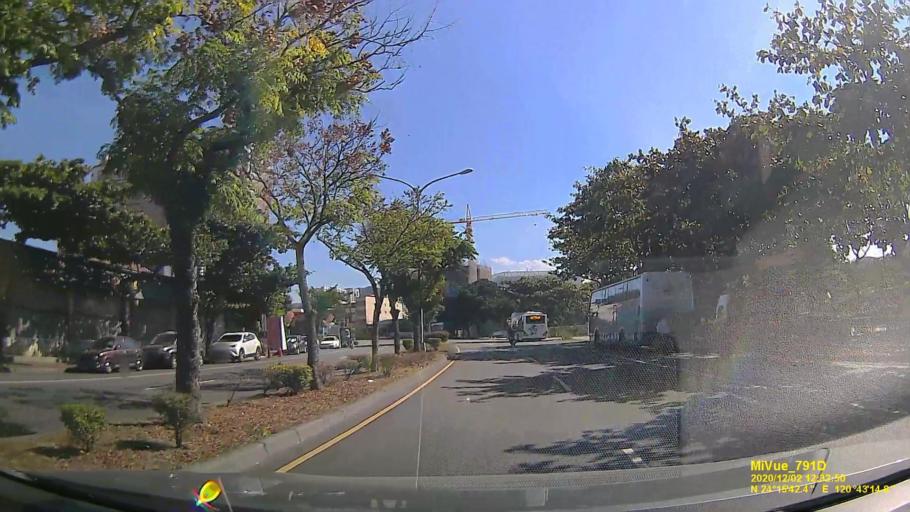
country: TW
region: Taiwan
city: Fengyuan
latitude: 24.2617
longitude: 120.7208
